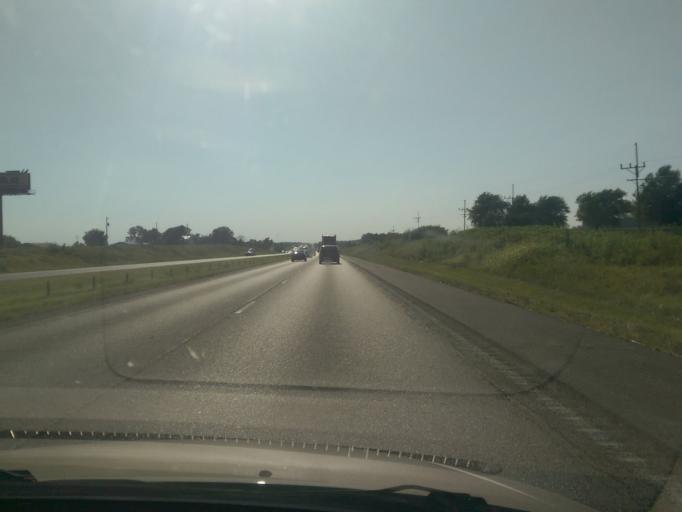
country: US
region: Missouri
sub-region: Lafayette County
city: Higginsville
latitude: 39.0018
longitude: -93.7620
